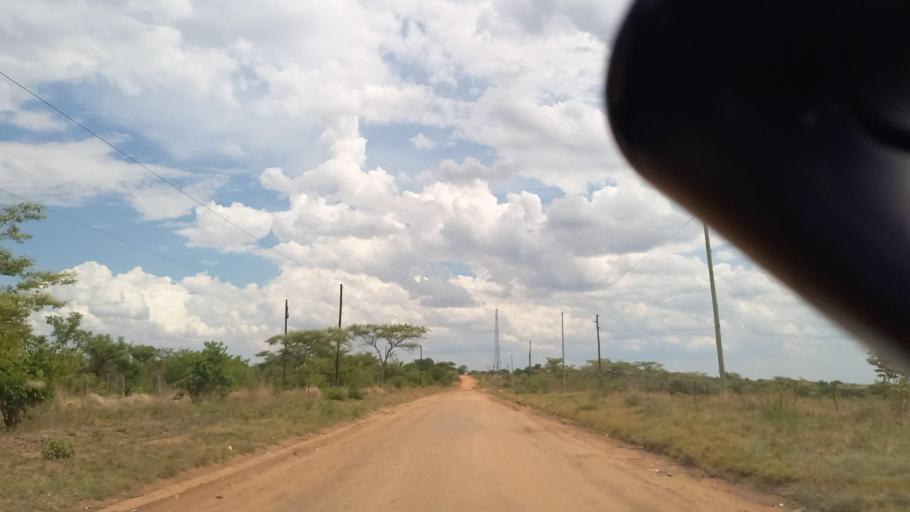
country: ZM
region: Southern
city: Nakambala
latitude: -16.0307
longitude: 27.9686
